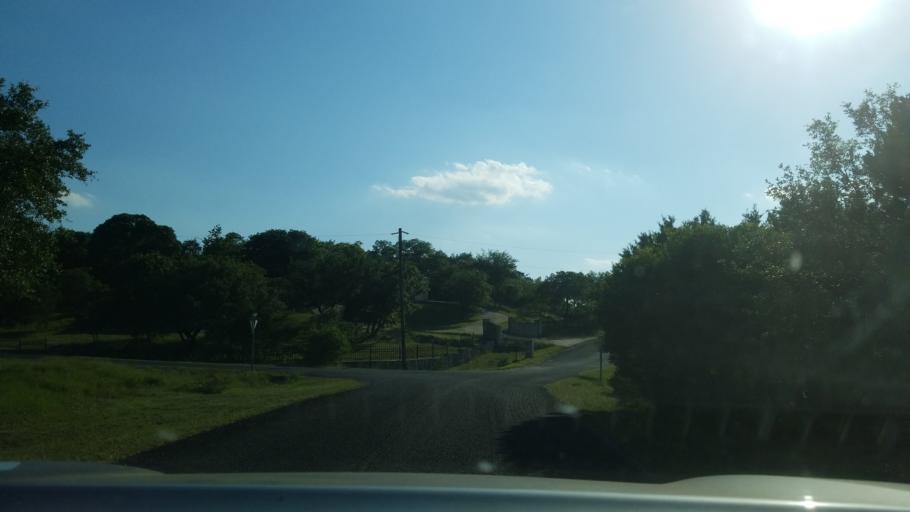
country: US
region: Texas
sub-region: Comal County
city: Bulverde
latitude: 29.7827
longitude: -98.4444
